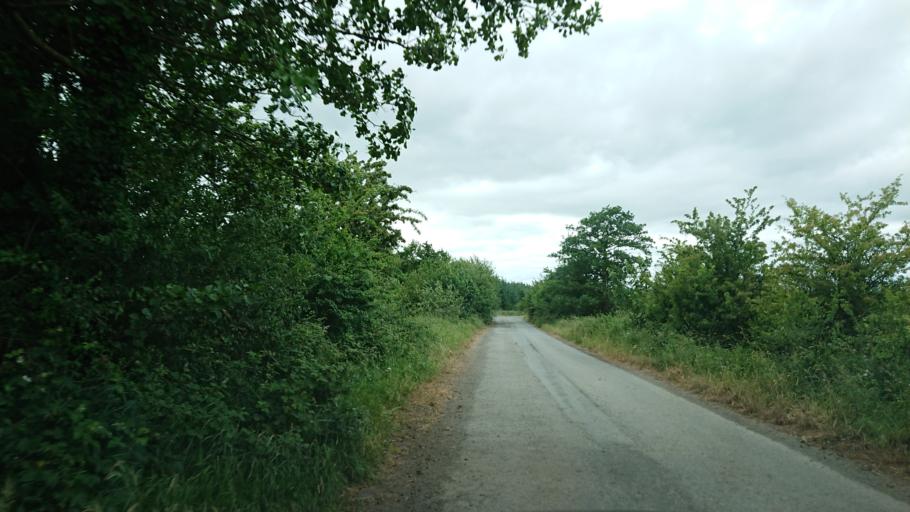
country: IE
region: Munster
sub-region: Waterford
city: Waterford
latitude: 52.2181
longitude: -7.1384
